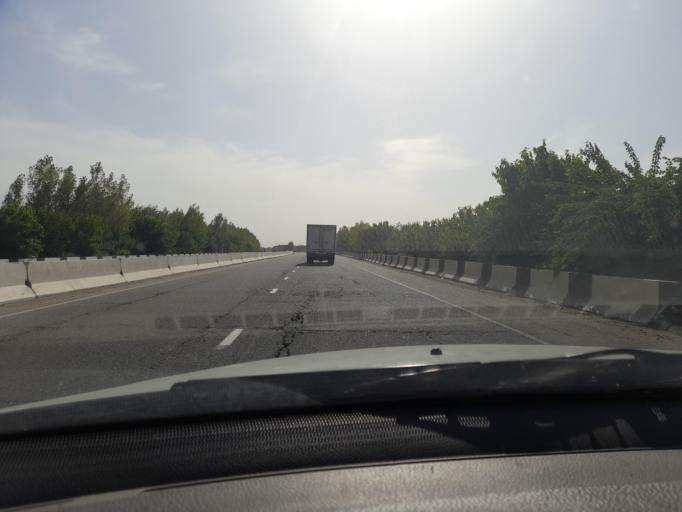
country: UZ
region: Samarqand
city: Ishtixon
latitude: 39.9442
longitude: 66.4041
